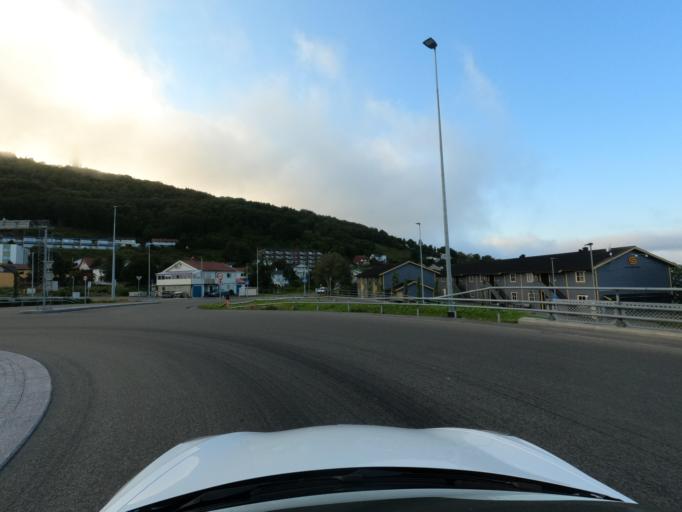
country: NO
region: Troms
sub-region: Harstad
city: Harstad
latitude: 68.8059
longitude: 16.5325
